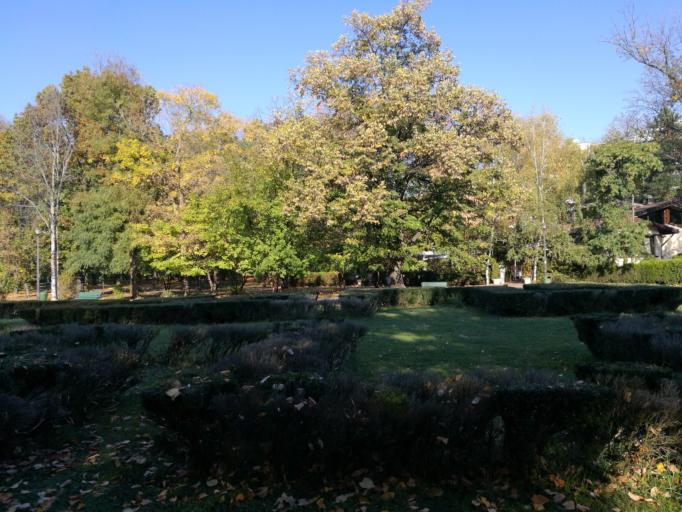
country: RO
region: Bucuresti
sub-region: Municipiul Bucuresti
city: Bucharest
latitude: 44.4804
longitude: 26.0852
